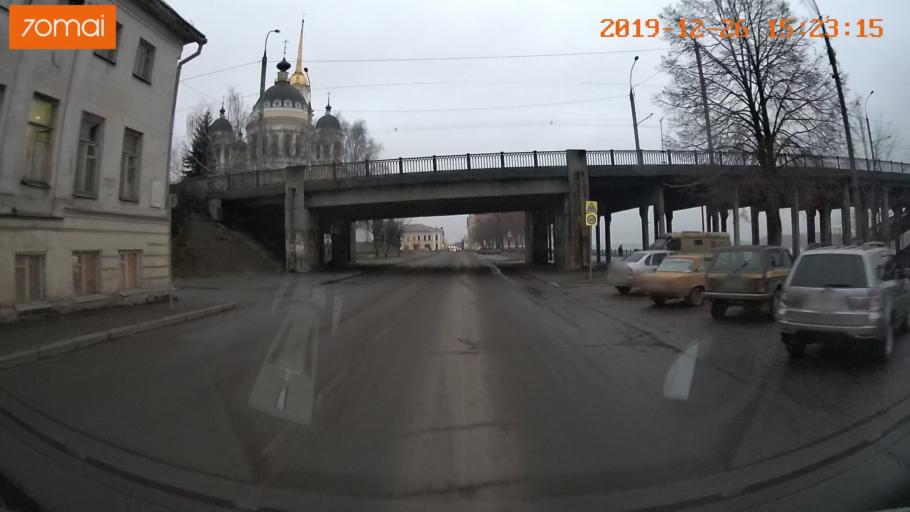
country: RU
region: Jaroslavl
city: Rybinsk
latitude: 58.0484
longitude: 38.8608
